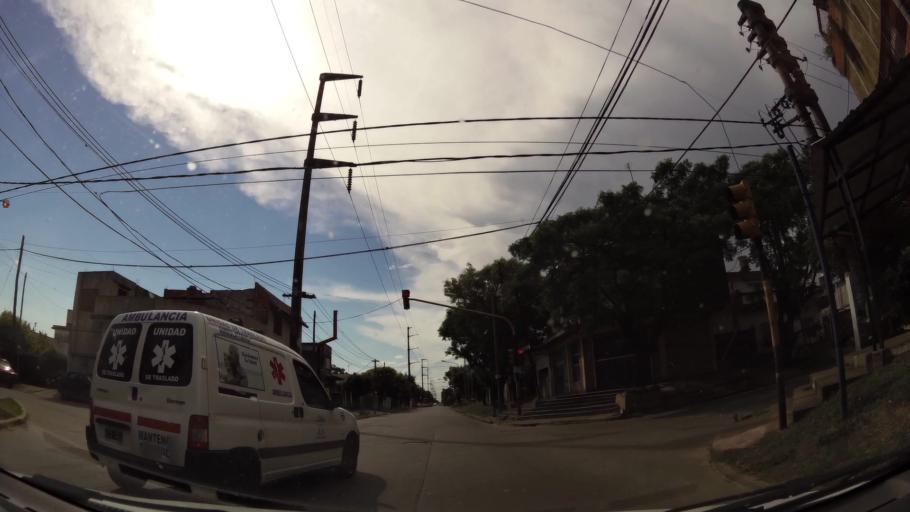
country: AR
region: Buenos Aires
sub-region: Partido de Merlo
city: Merlo
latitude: -34.6424
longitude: -58.6944
